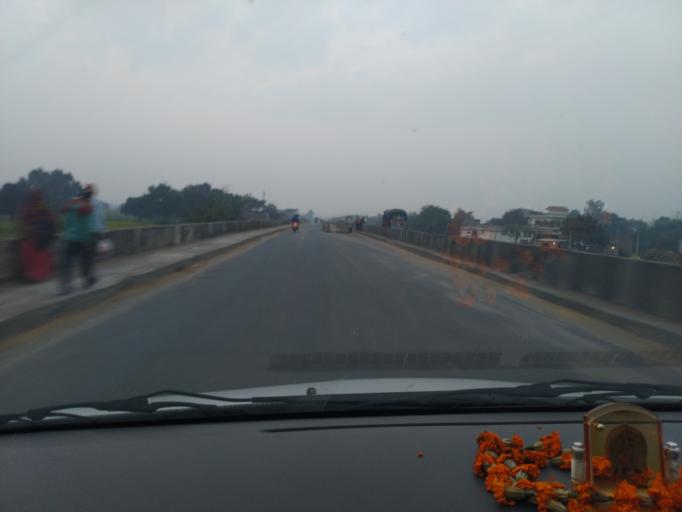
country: IN
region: Bihar
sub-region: Kaimur District
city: Bhabua
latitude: 25.2144
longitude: 83.5135
